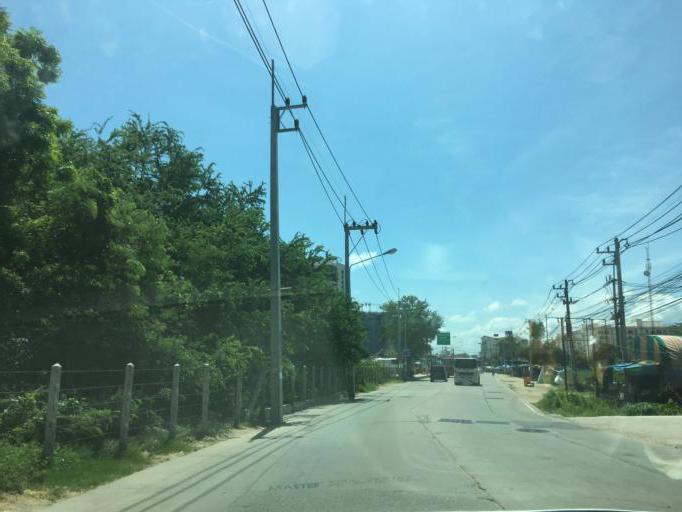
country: TH
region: Chon Buri
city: Phatthaya
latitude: 12.8891
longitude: 100.8823
